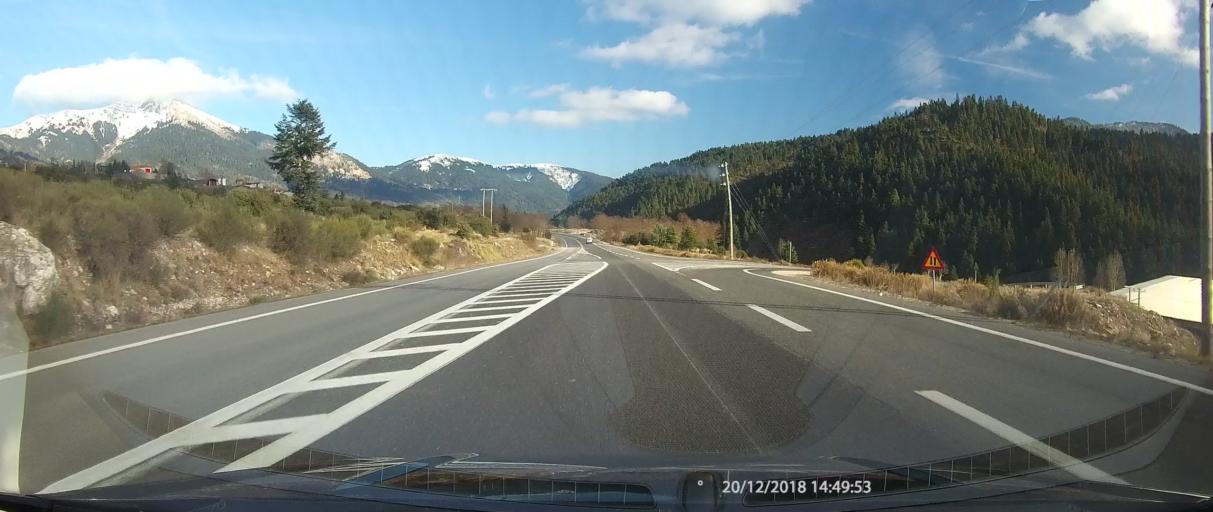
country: GR
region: Central Greece
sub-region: Nomos Evrytanias
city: Karpenisi
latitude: 38.9046
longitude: 21.8133
